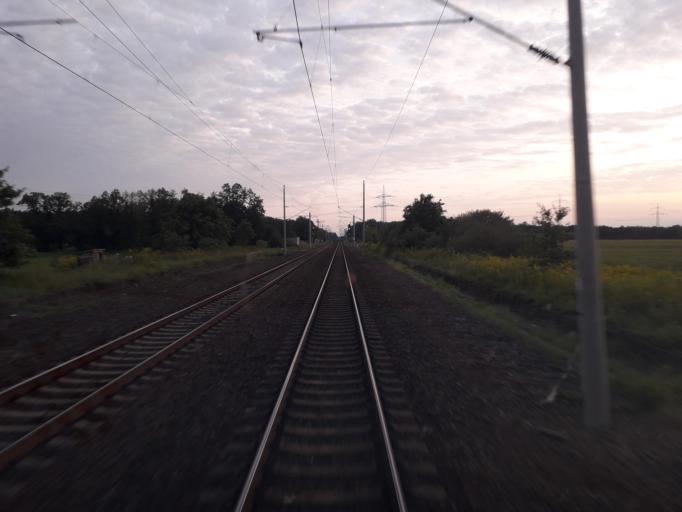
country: DE
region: Brandenburg
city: Falkensee
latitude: 52.6305
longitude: 13.1241
